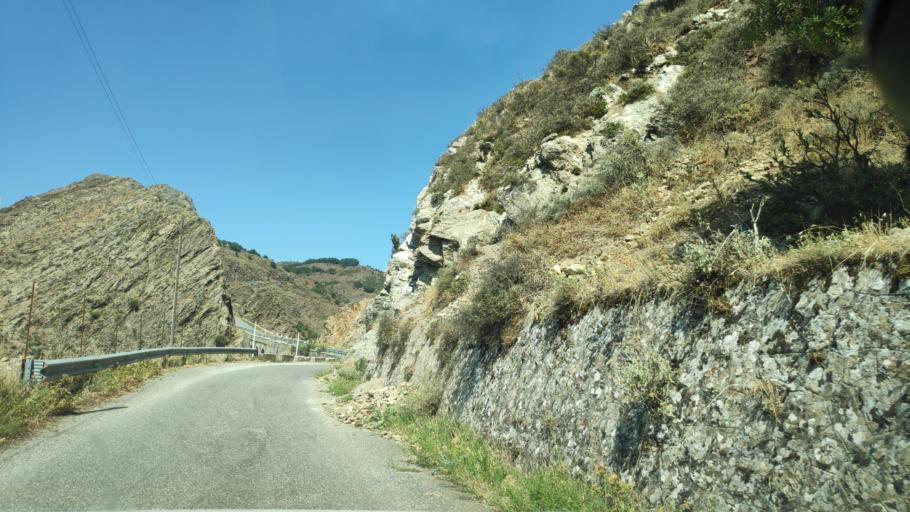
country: IT
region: Calabria
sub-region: Provincia di Reggio Calabria
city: Bova
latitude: 38.0065
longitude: 15.9315
